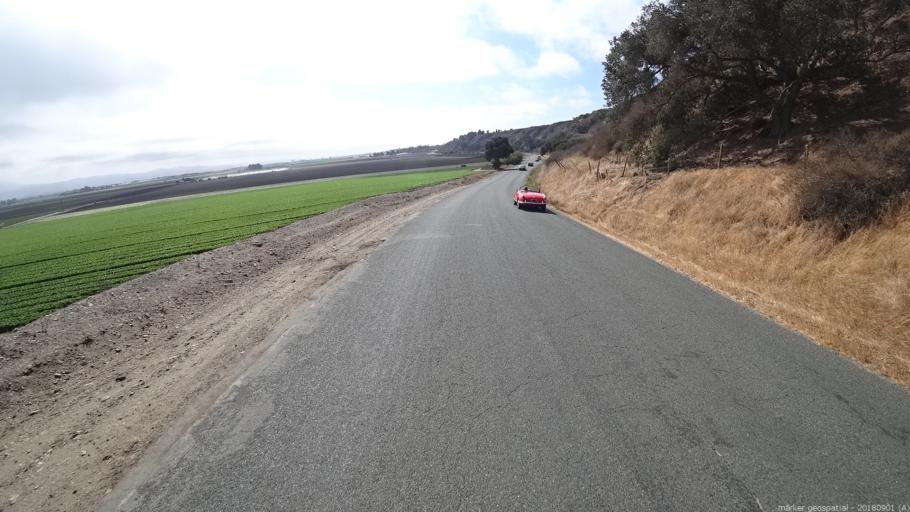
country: US
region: California
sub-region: Monterey County
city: Soledad
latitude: 36.4049
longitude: -121.3808
